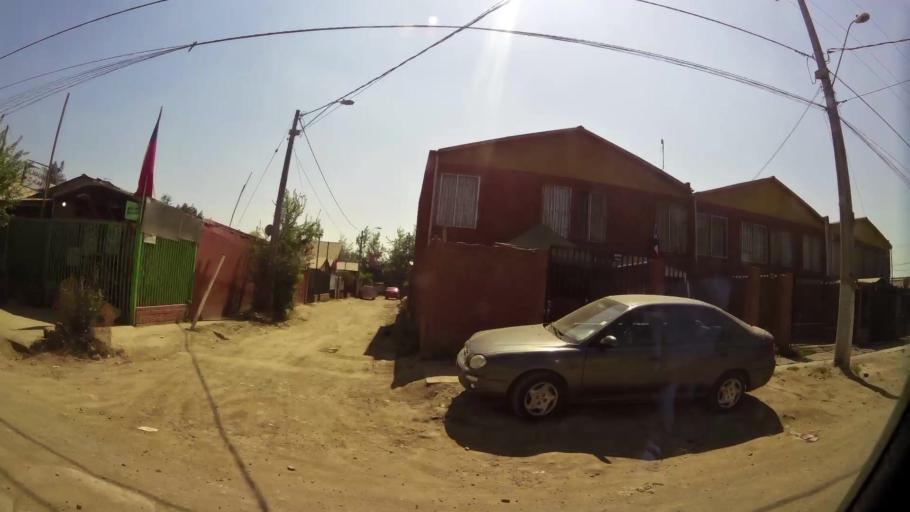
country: CL
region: Santiago Metropolitan
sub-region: Provincia de Talagante
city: Penaflor
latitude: -33.5850
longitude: -70.8092
